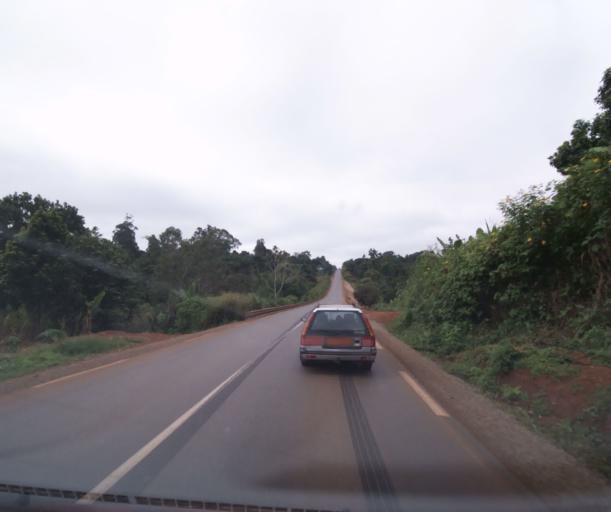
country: CM
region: West
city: Mbouda
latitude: 5.5723
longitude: 10.3096
